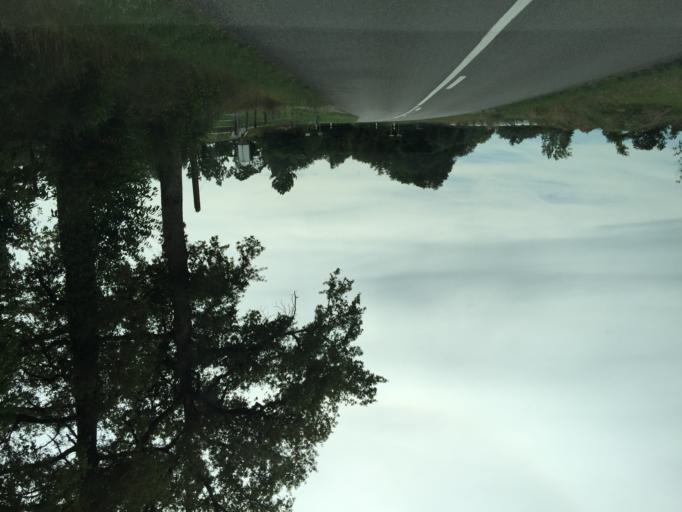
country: FR
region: Midi-Pyrenees
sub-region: Departement de l'Aveyron
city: La Fouillade
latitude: 44.2601
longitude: 2.0305
